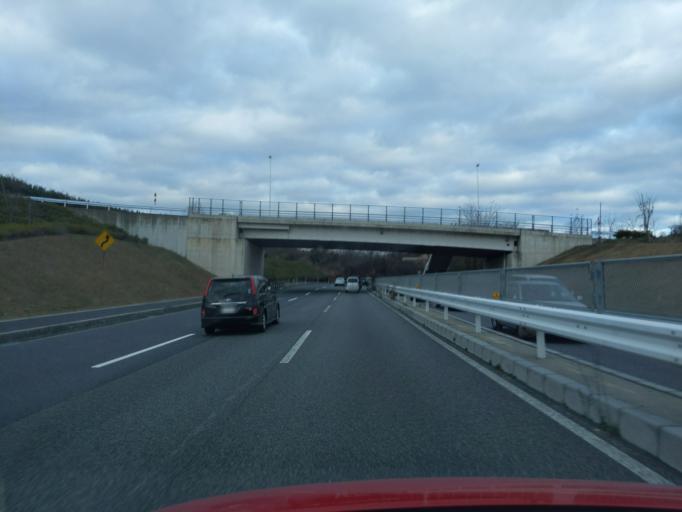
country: JP
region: Gifu
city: Tajimi
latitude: 35.3418
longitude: 137.1431
